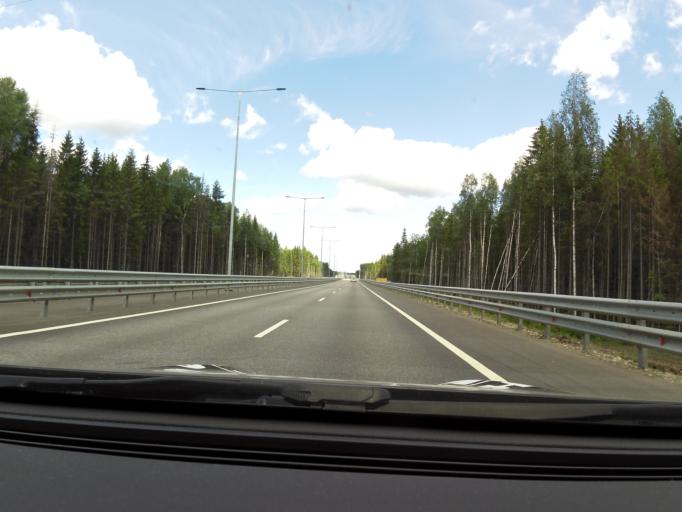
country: RU
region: Tverskaya
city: Krasnomayskiy
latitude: 57.6145
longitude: 34.2461
